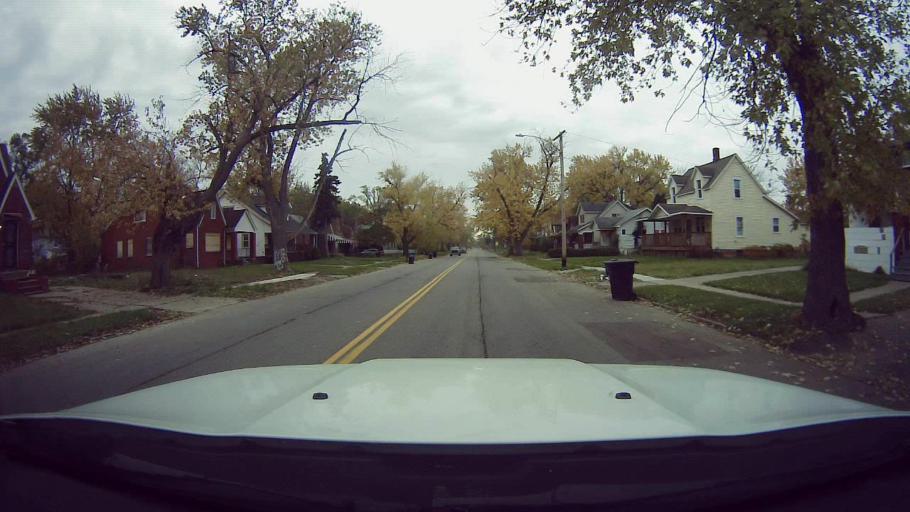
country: US
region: Michigan
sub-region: Oakland County
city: Oak Park
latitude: 42.3964
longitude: -83.1887
